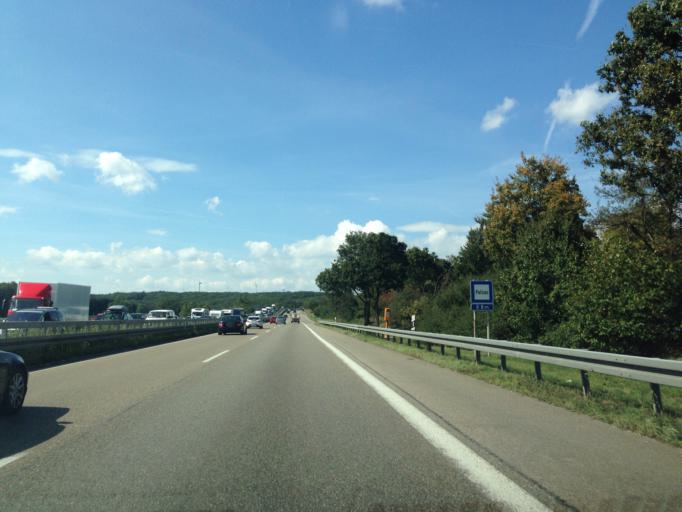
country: DE
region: Baden-Wuerttemberg
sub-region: Regierungsbezirk Stuttgart
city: Hohenstadt
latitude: 48.5332
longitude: 9.6650
